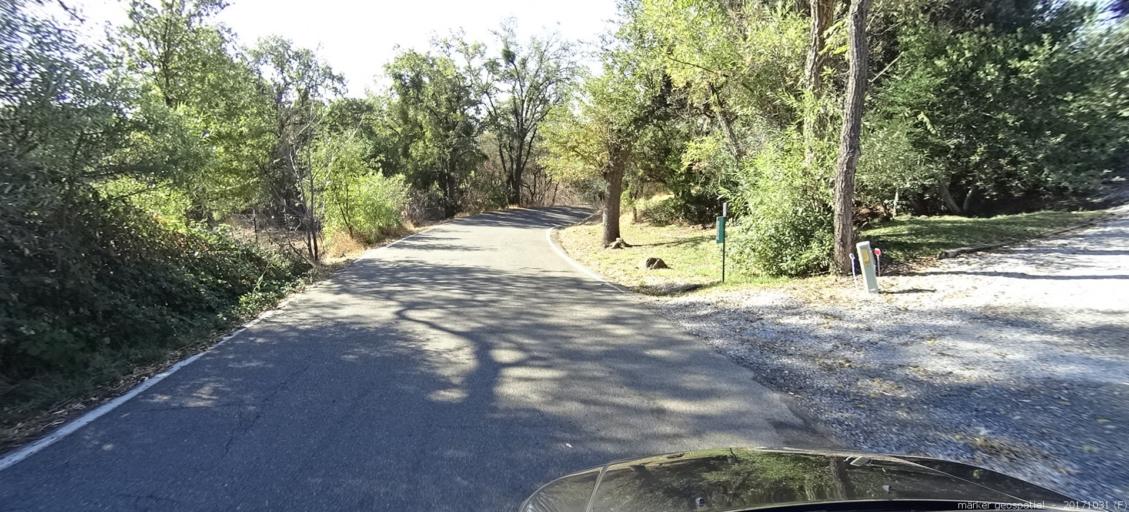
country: US
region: California
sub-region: Shasta County
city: Shingletown
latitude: 40.4623
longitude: -121.8896
